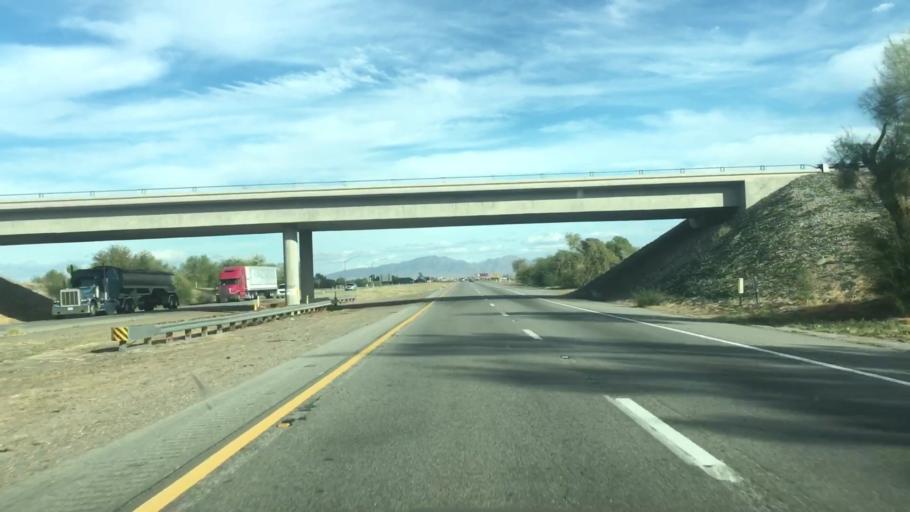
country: US
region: California
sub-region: Riverside County
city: Blythe
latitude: 33.6066
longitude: -114.6582
